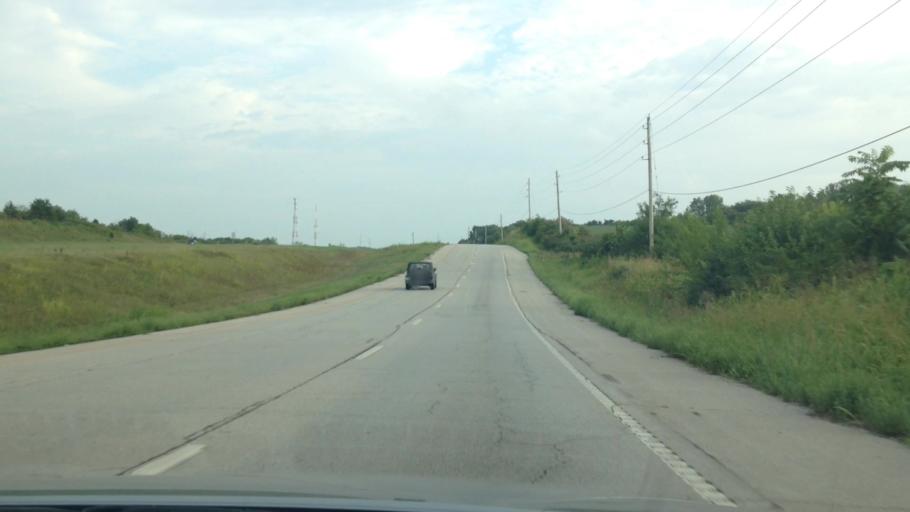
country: US
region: Missouri
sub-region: Clay County
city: Smithville
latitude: 39.3465
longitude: -94.5840
